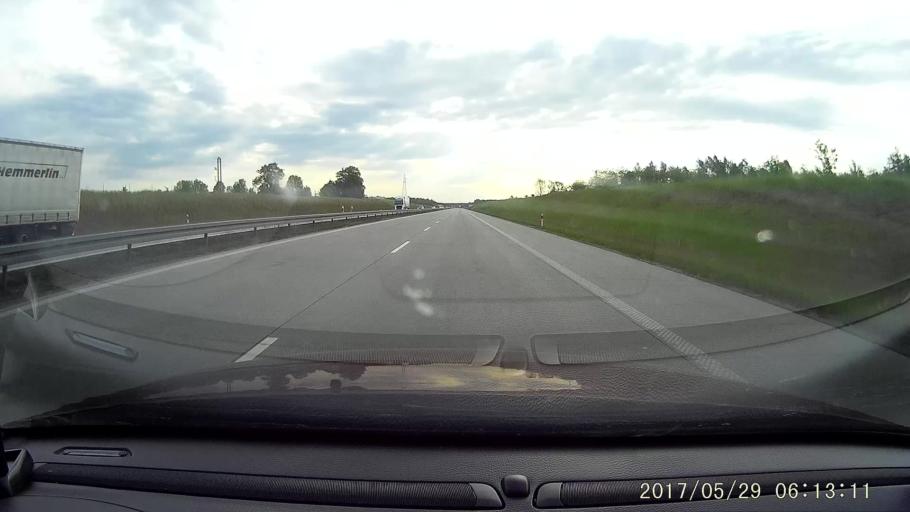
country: PL
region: Lower Silesian Voivodeship
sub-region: Powiat zgorzelecki
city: Wegliniec
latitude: 51.2252
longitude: 15.2956
